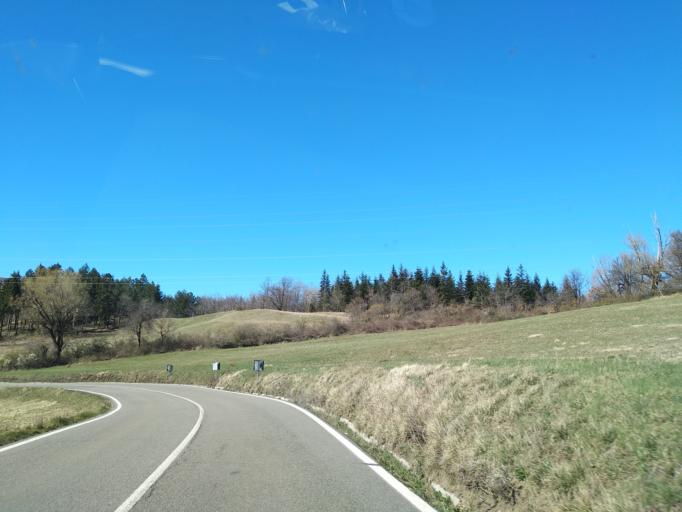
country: IT
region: Emilia-Romagna
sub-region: Provincia di Reggio Emilia
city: Busana
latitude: 44.4082
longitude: 10.3389
